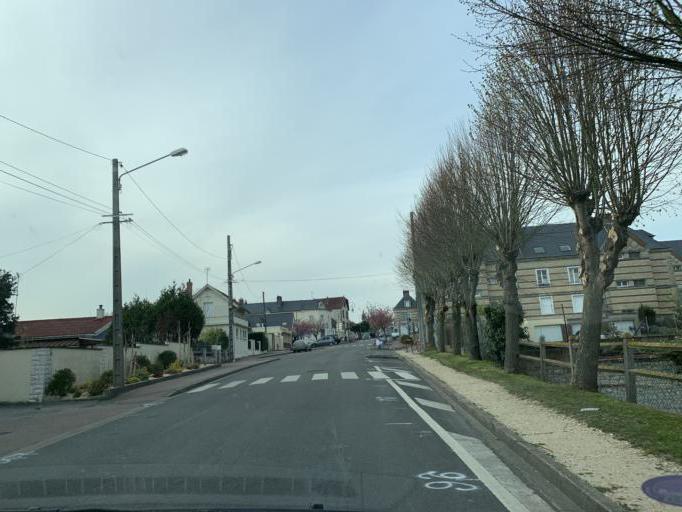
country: FR
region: Haute-Normandie
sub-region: Departement de la Seine-Maritime
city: La Mailleraye-sur-Seine
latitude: 49.4810
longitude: 0.7723
